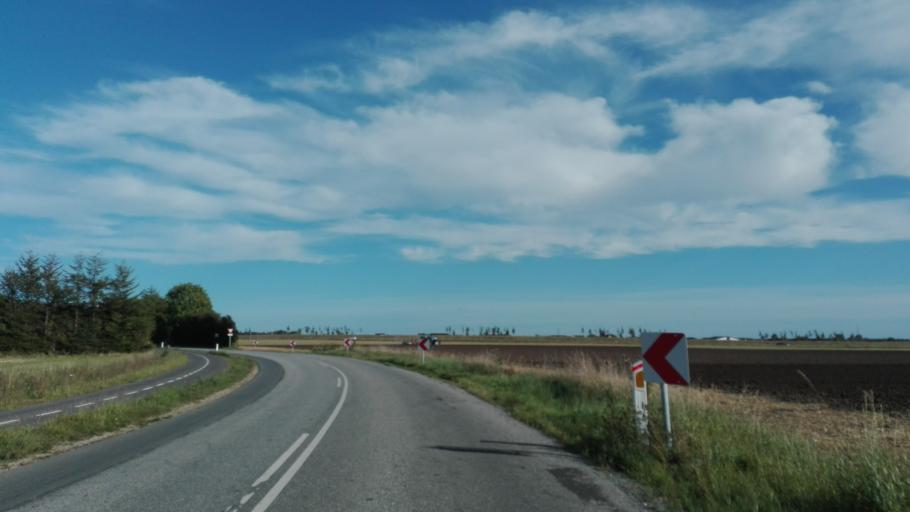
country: DK
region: South Denmark
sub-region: Fredericia Kommune
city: Fredericia
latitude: 55.5826
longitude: 9.6925
